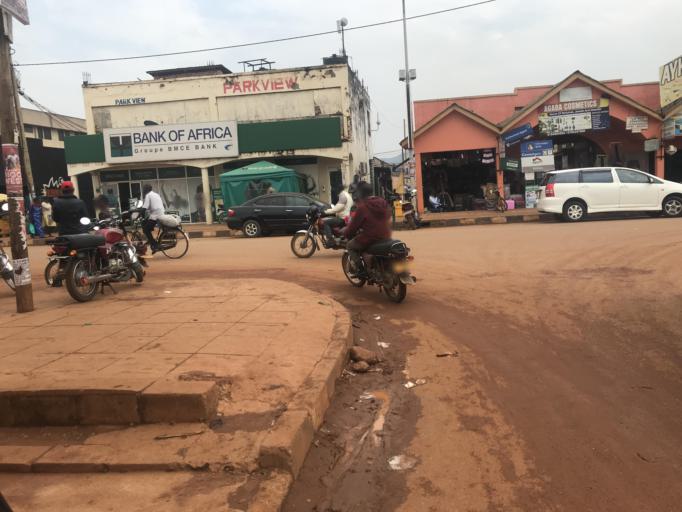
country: UG
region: Western Region
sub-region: Hoima District
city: Hoima
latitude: 1.4318
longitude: 31.3509
